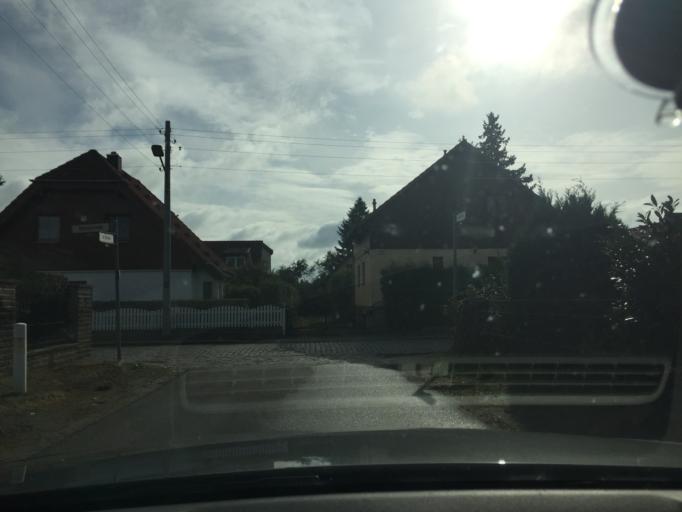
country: DE
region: Berlin
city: Hellersdorf
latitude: 52.5271
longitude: 13.6339
